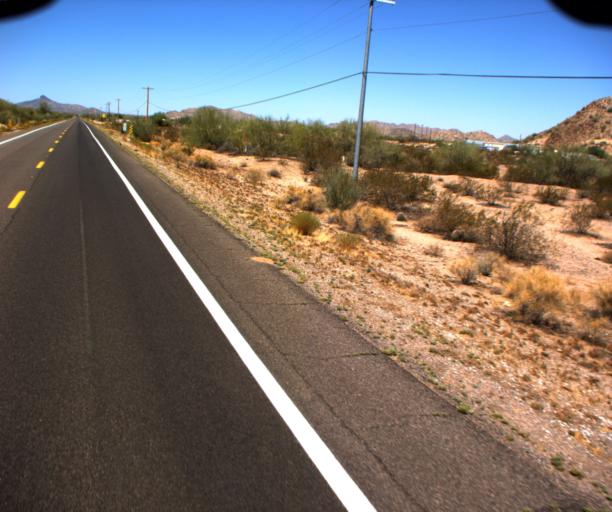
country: US
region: Arizona
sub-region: Pinal County
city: Maricopa
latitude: 32.8670
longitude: -112.0636
